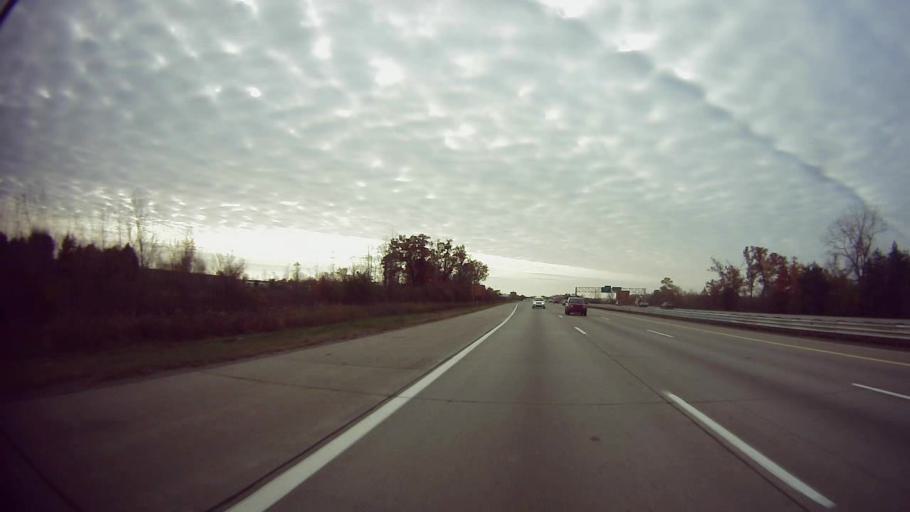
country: US
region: Michigan
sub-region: Wayne County
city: Woodhaven
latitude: 42.1776
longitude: -83.2432
